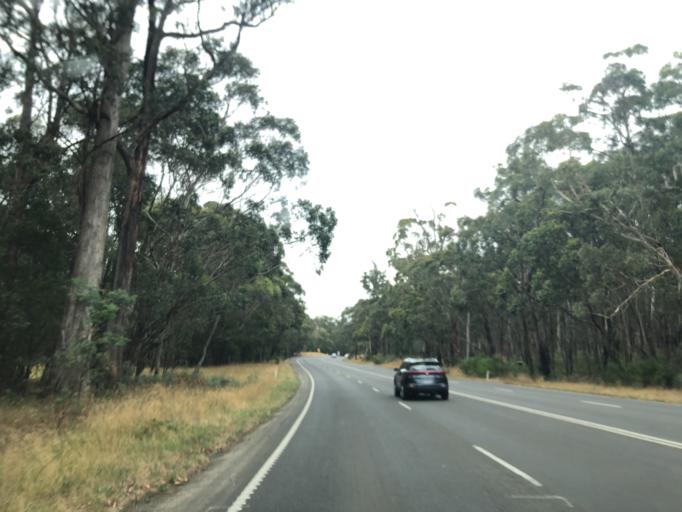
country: AU
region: Victoria
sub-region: Hume
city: Sunbury
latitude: -37.3926
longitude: 144.5272
